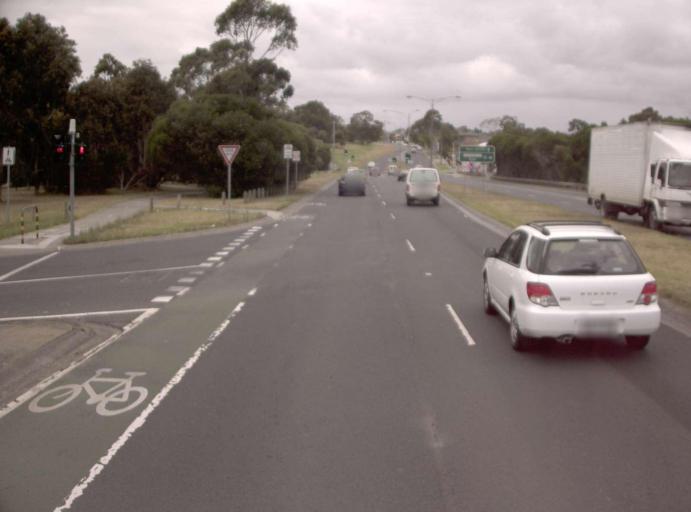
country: AU
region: Victoria
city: Alphington
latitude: -37.7919
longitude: 145.0298
